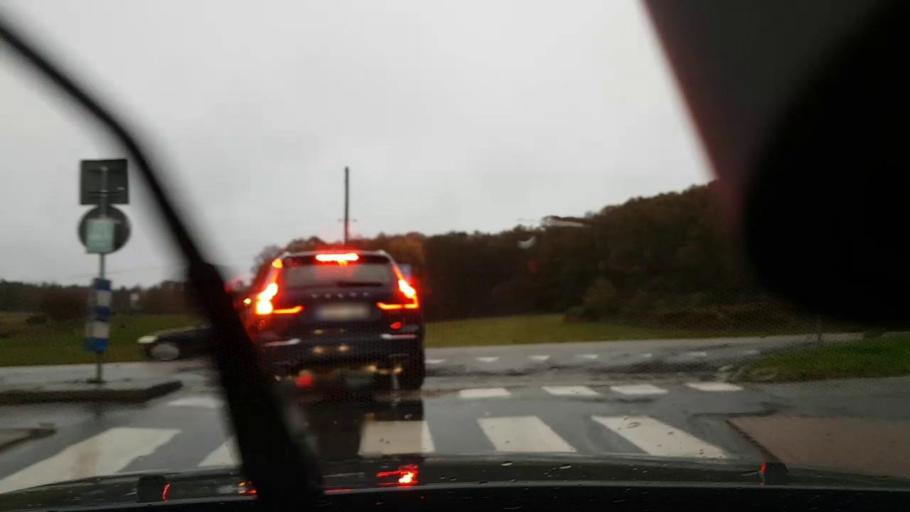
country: SE
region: Vaestra Goetaland
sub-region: Molndal
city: Lindome
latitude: 57.5823
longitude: 12.1058
